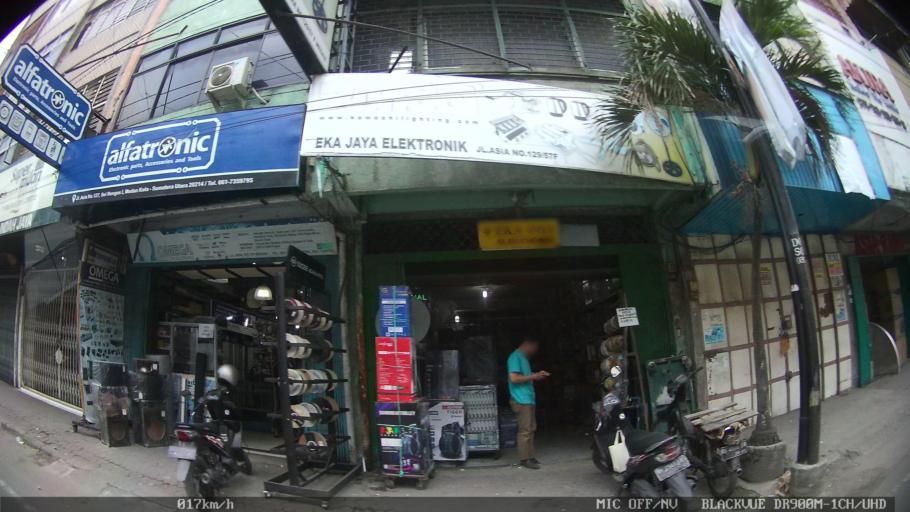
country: ID
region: North Sumatra
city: Medan
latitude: 3.5847
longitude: 98.6912
